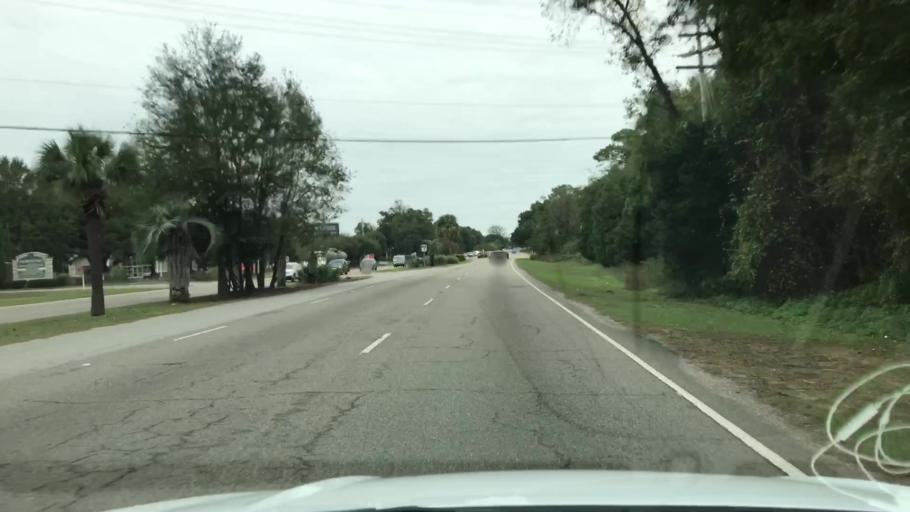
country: US
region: South Carolina
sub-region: Georgetown County
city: Murrells Inlet
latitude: 33.4783
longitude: -79.1005
